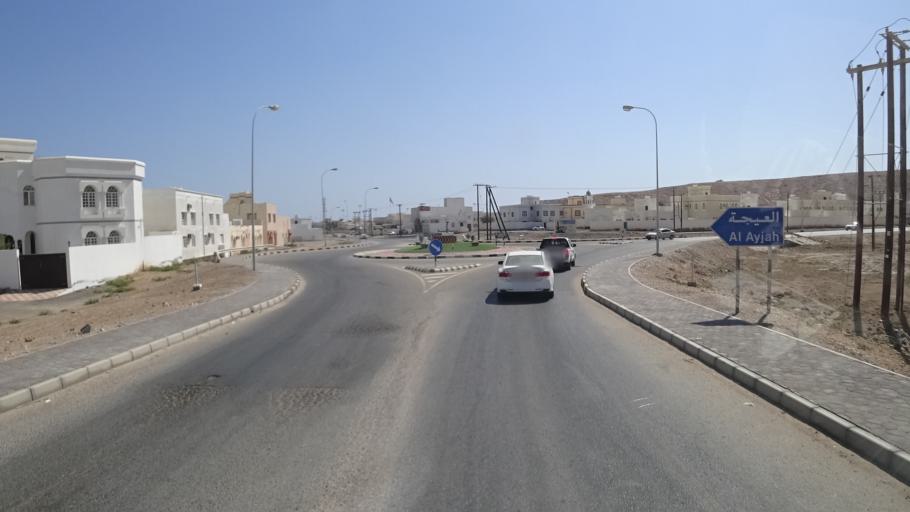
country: OM
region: Ash Sharqiyah
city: Sur
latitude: 22.5635
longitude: 59.5425
